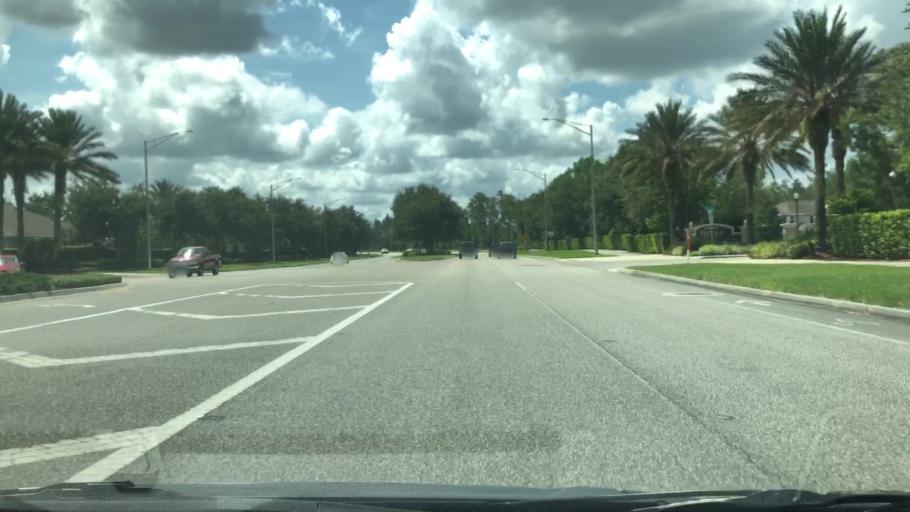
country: US
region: Florida
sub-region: Saint Johns County
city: Fruit Cove
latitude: 30.1330
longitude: -81.5440
